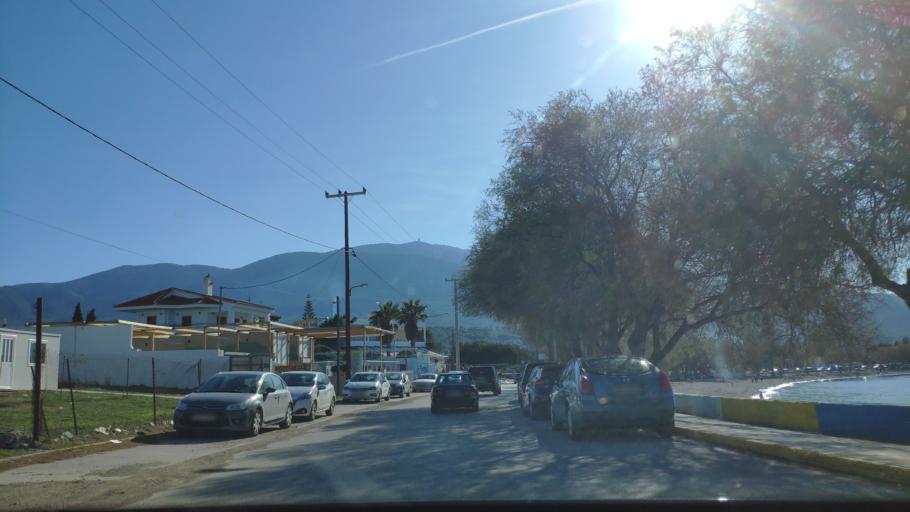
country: GR
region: Attica
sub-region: Nomarchia Dytikis Attikis
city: Kineta
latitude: 38.0746
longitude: 23.1712
